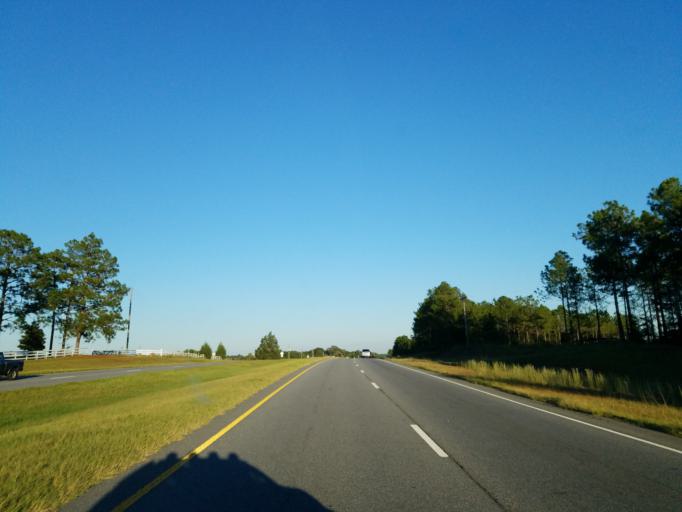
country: US
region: Georgia
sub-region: Worth County
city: Sylvester
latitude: 31.5107
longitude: -83.7551
